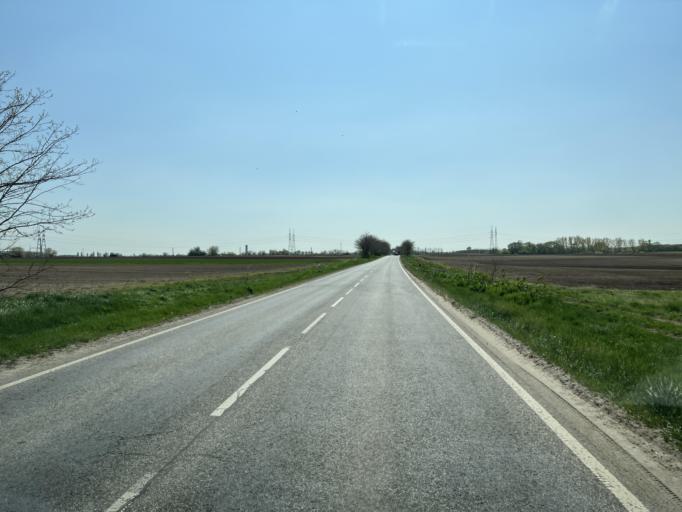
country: HU
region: Pest
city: Alsonemedi
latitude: 47.3213
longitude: 19.1963
